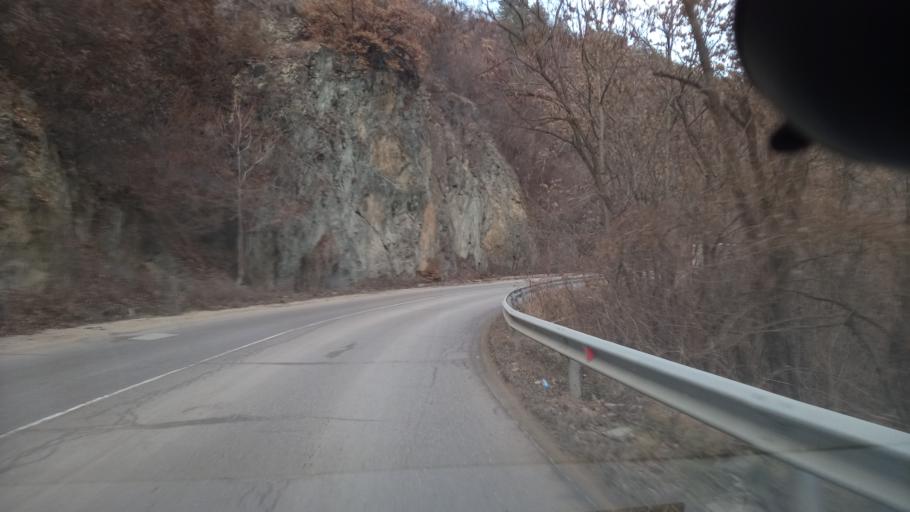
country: BG
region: Sofia-Capital
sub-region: Stolichna Obshtina
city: Sofia
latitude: 42.5671
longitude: 23.4236
